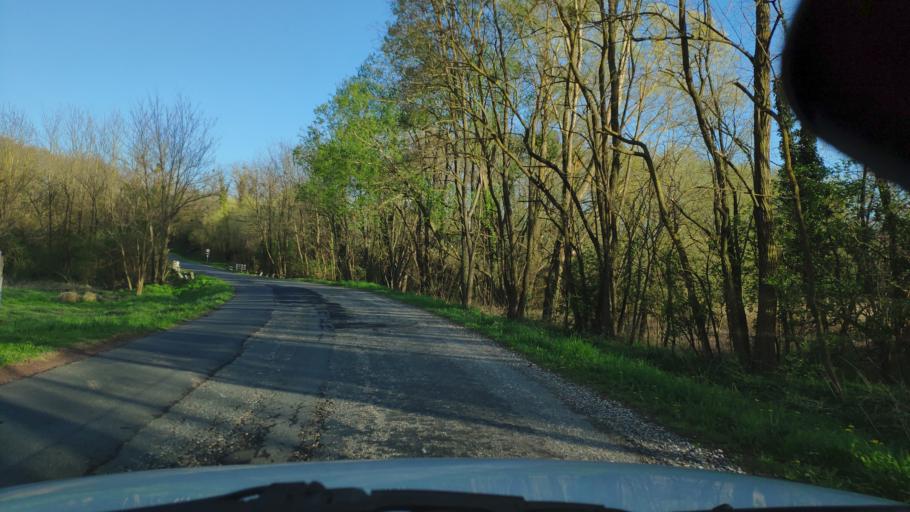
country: HU
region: Zala
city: Zalakomar
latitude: 46.4398
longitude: 17.1231
